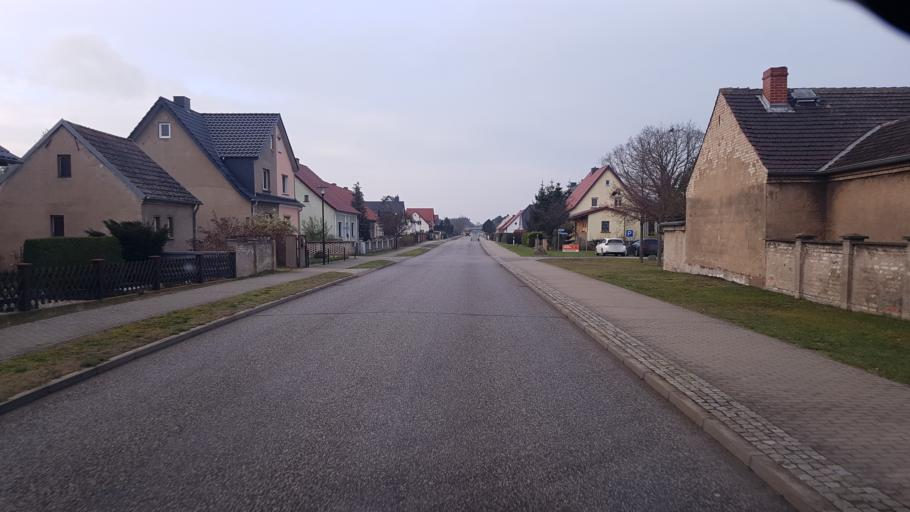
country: DE
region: Brandenburg
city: Vogelsang
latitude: 52.1826
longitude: 14.6627
